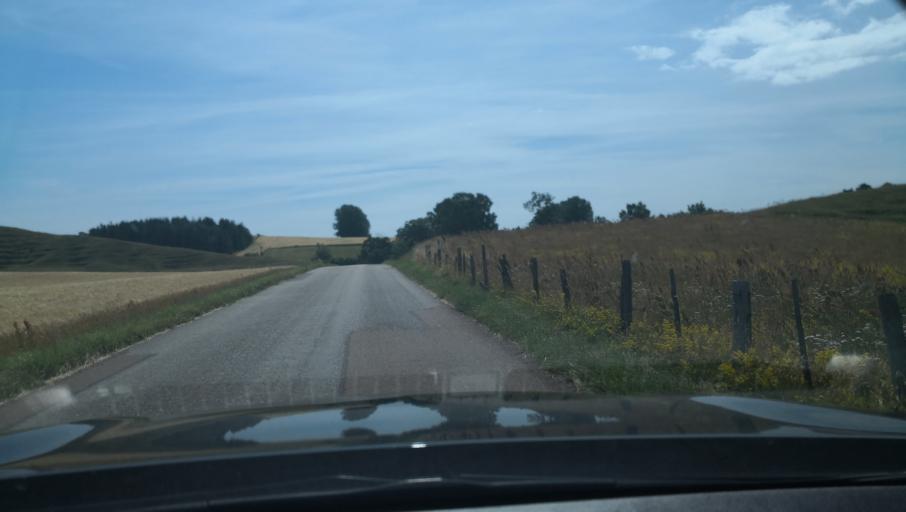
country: SE
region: Skane
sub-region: Ystads Kommun
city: Kopingebro
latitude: 55.3938
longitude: 14.1380
